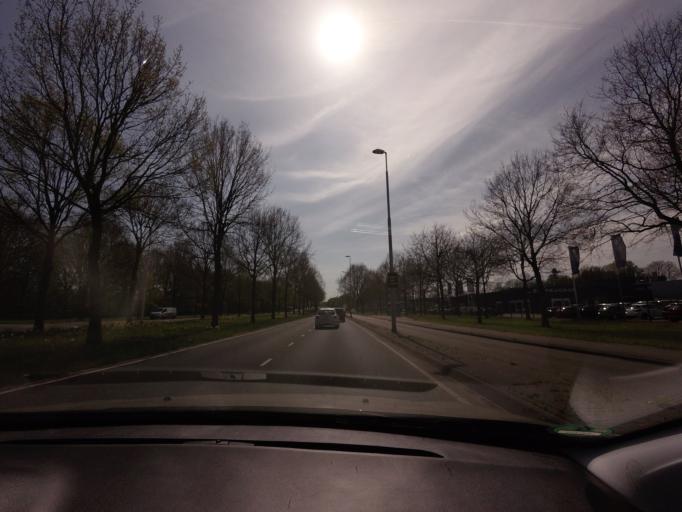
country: NL
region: North Brabant
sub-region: Gemeente Tilburg
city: Tilburg
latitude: 51.5830
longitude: 5.0672
